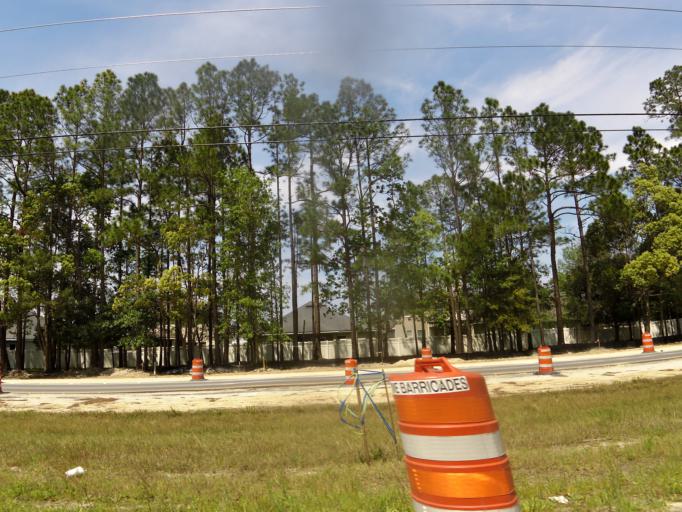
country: US
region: Florida
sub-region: Nassau County
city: Yulee
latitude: 30.5197
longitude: -81.6516
